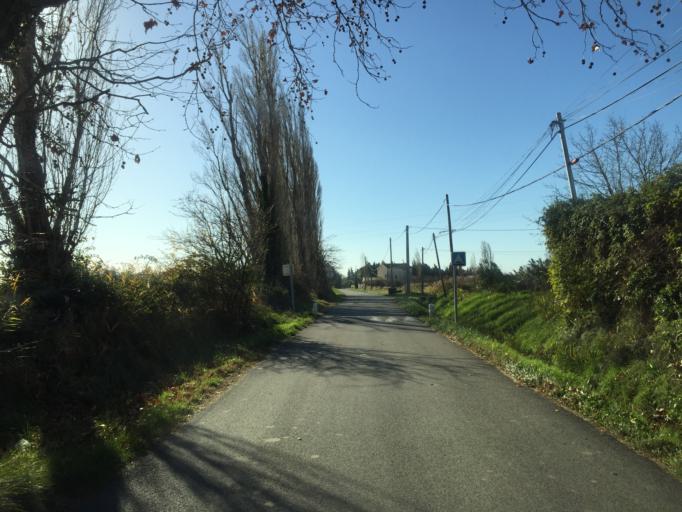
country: FR
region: Provence-Alpes-Cote d'Azur
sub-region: Departement du Vaucluse
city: Bedarrides
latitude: 44.0539
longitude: 4.9049
